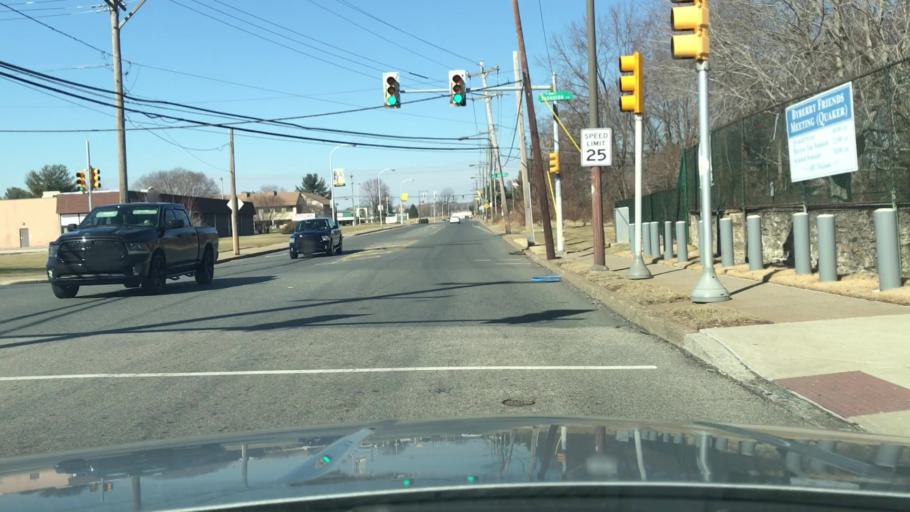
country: US
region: Pennsylvania
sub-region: Bucks County
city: Trevose
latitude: 40.1023
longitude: -74.9818
